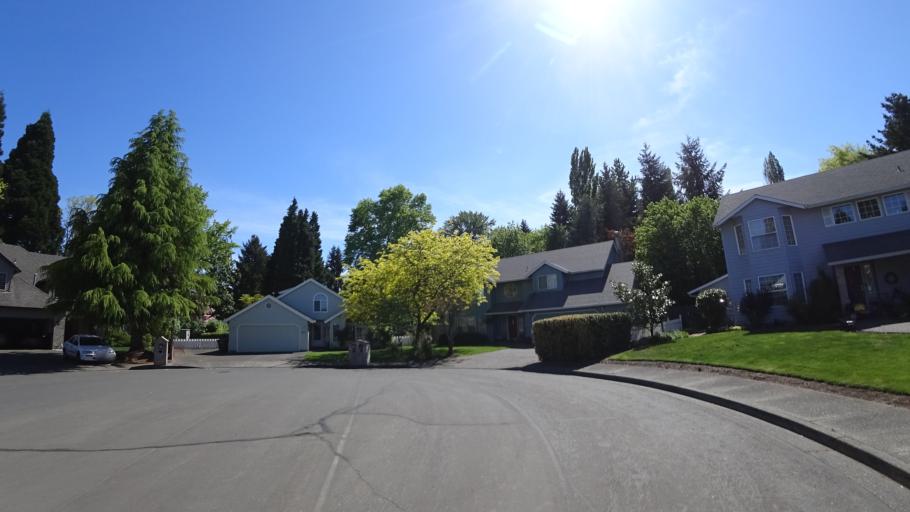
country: US
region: Oregon
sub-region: Washington County
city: Hillsboro
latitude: 45.5128
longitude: -122.9508
